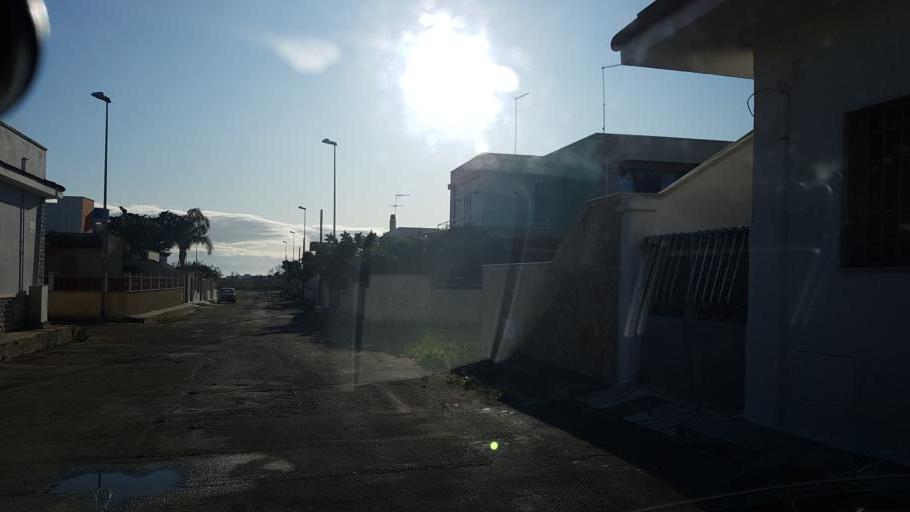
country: IT
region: Apulia
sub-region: Provincia di Brindisi
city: Torchiarolo
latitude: 40.5348
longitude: 18.0707
